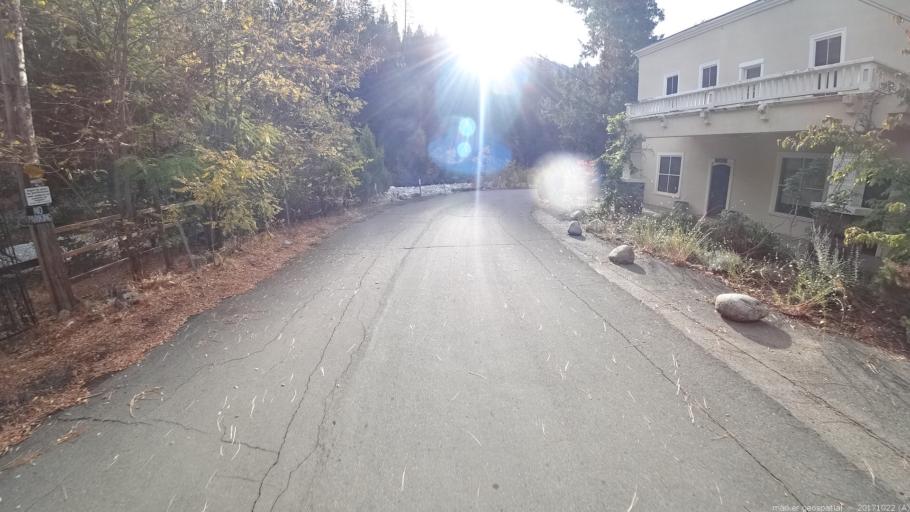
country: US
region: California
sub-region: Siskiyou County
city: Dunsmuir
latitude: 41.1447
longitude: -122.3145
